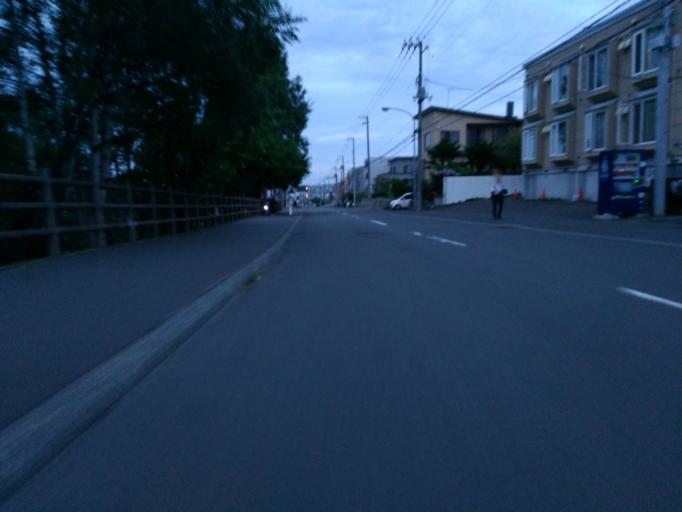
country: JP
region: Hokkaido
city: Ebetsu
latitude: 43.0661
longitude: 141.4983
